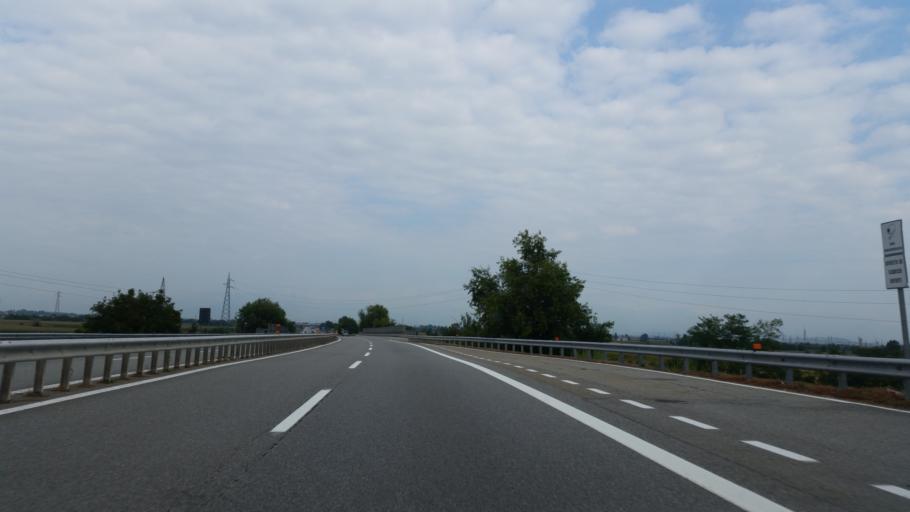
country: IT
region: Piedmont
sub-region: Provincia di Torino
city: Verolengo
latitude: 45.2065
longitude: 7.9512
